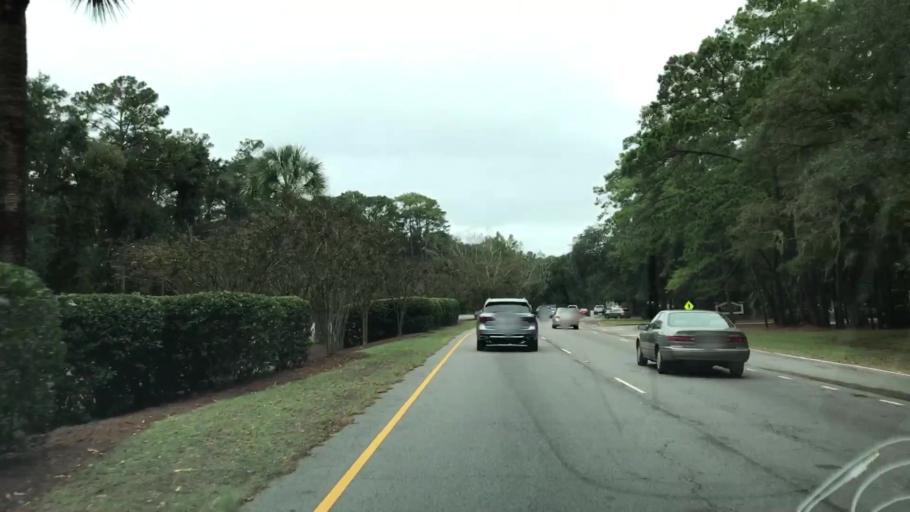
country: US
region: South Carolina
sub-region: Beaufort County
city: Hilton Head Island
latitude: 32.2137
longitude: -80.7227
